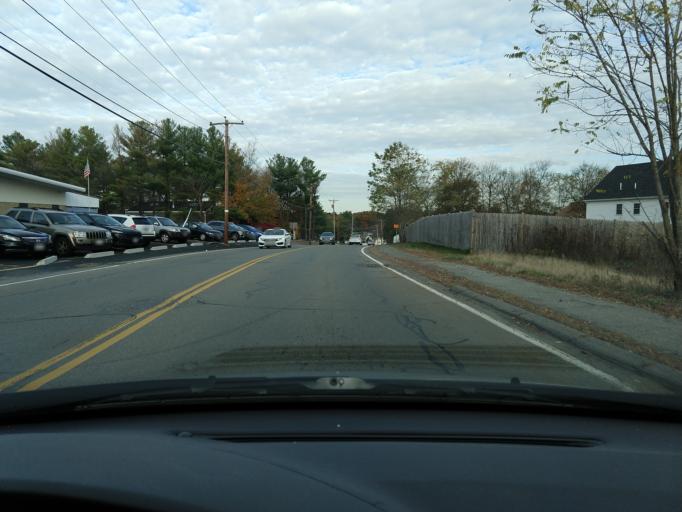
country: US
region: Massachusetts
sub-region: Middlesex County
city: Billerica
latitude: 42.5533
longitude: -71.2630
